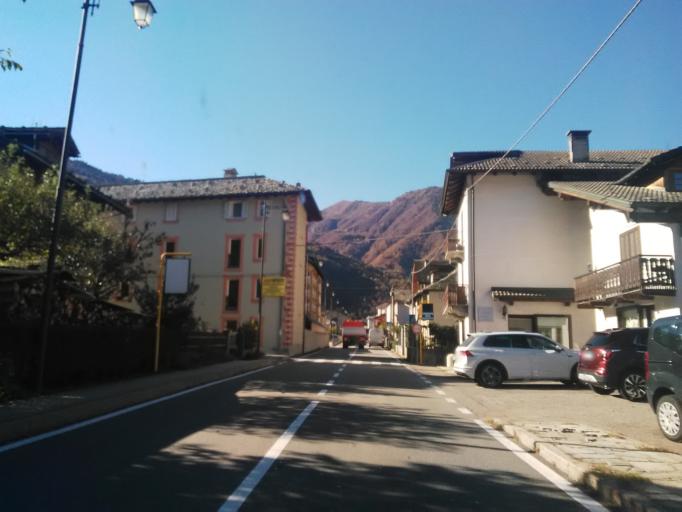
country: IT
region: Piedmont
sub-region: Provincia di Vercelli
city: Scopello
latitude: 45.7755
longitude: 8.0963
